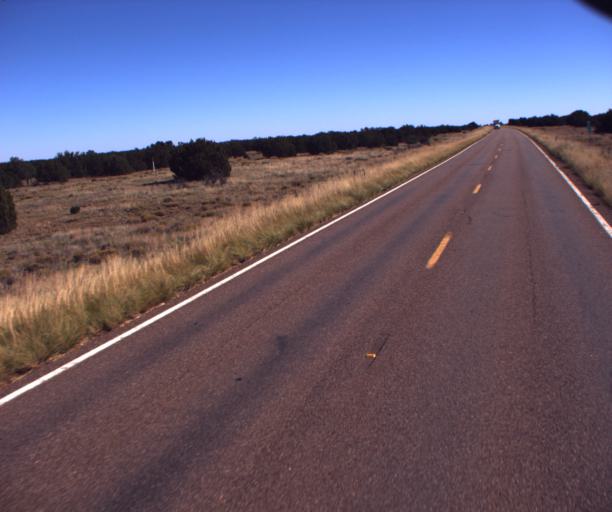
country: US
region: Arizona
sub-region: Navajo County
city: Heber-Overgaard
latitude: 34.4613
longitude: -110.3893
